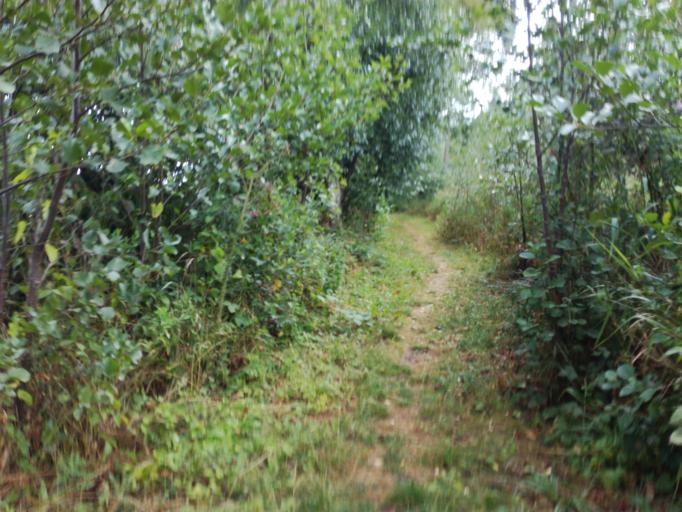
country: DK
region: South Denmark
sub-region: Vejle Kommune
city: Brejning
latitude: 55.6321
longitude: 9.7295
